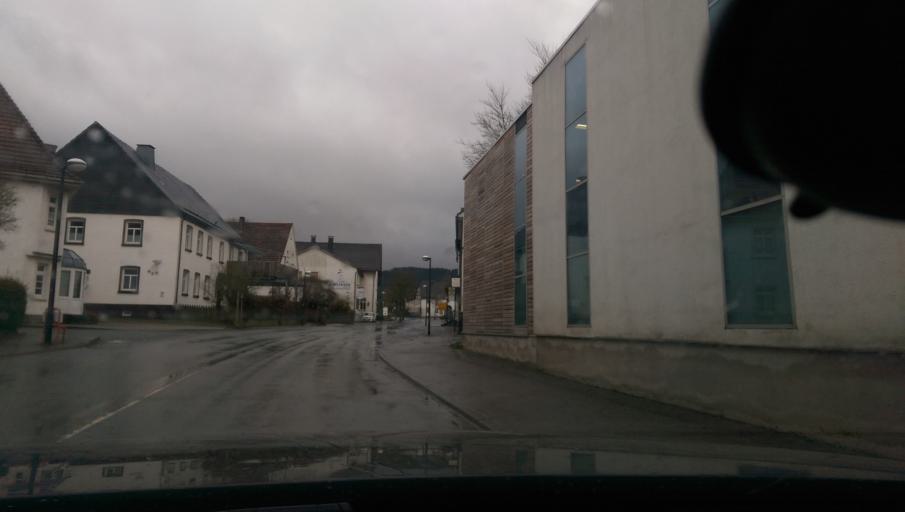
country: DE
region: North Rhine-Westphalia
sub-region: Regierungsbezirk Arnsberg
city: Sundern
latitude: 51.2834
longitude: 7.9507
